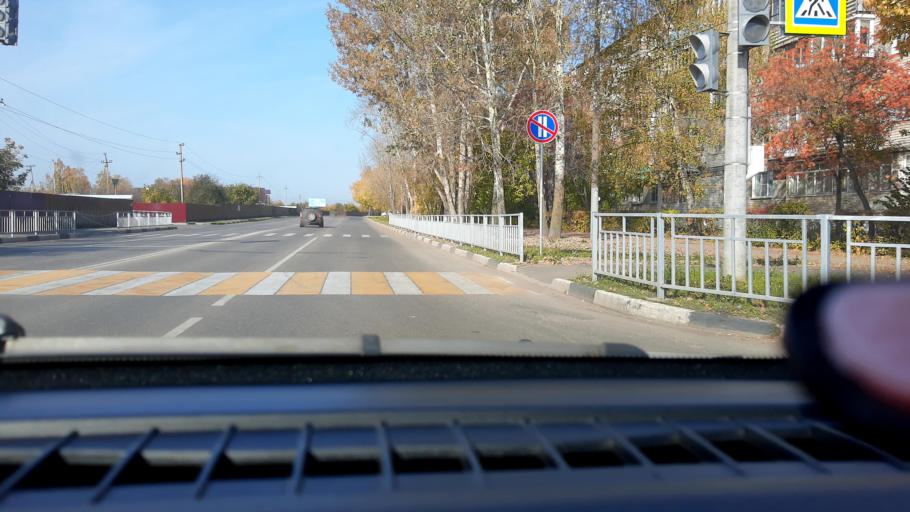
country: RU
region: Nizjnij Novgorod
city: Kstovo
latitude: 56.1428
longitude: 44.1824
